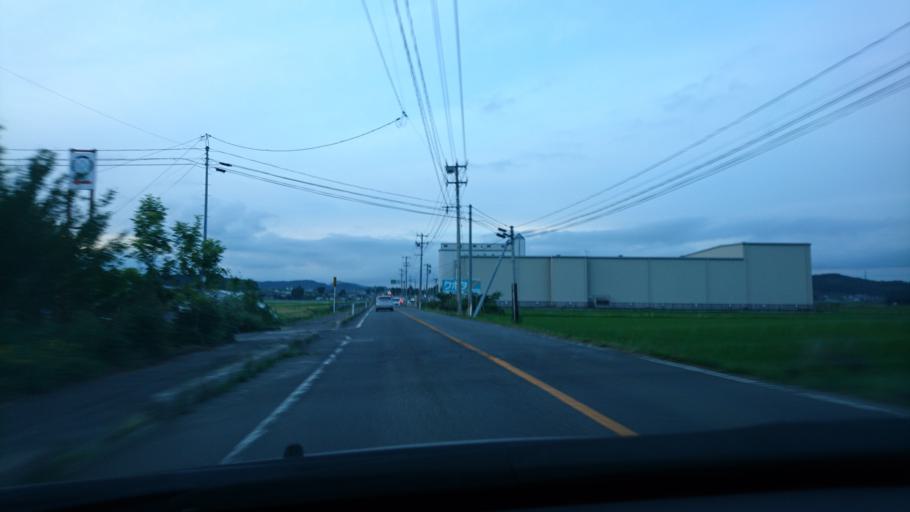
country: JP
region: Iwate
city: Ichinoseki
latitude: 38.8010
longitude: 140.9807
